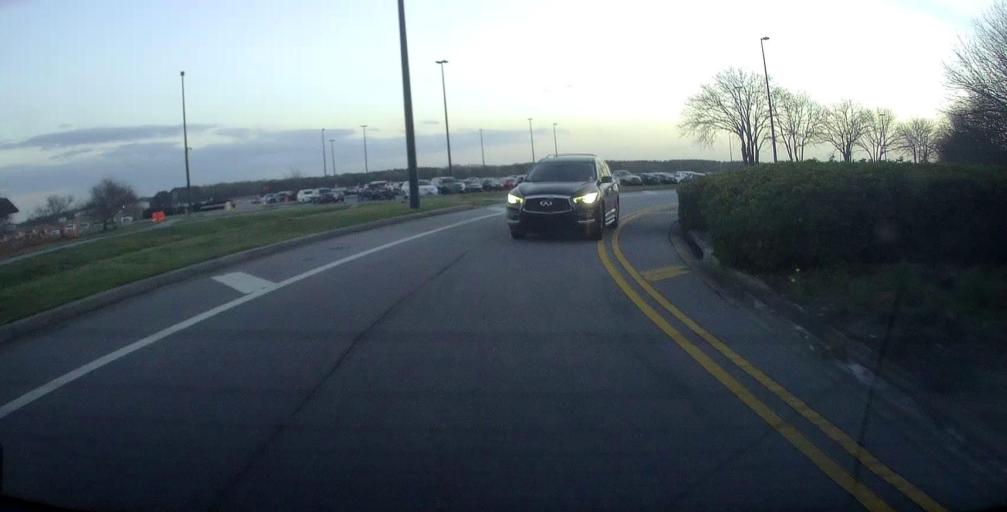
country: US
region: Georgia
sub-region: Chatham County
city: Pooler
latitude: 32.1340
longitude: -81.2104
